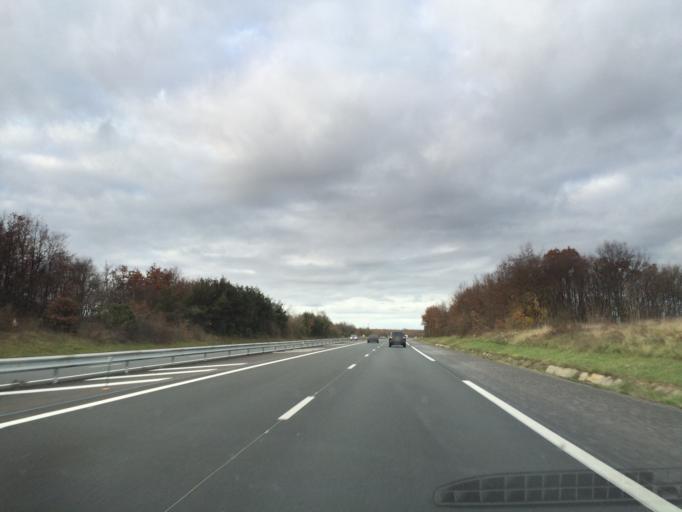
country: FR
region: Poitou-Charentes
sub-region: Departement des Deux-Sevres
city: Beauvoir-sur-Niort
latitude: 46.0936
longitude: -0.5335
